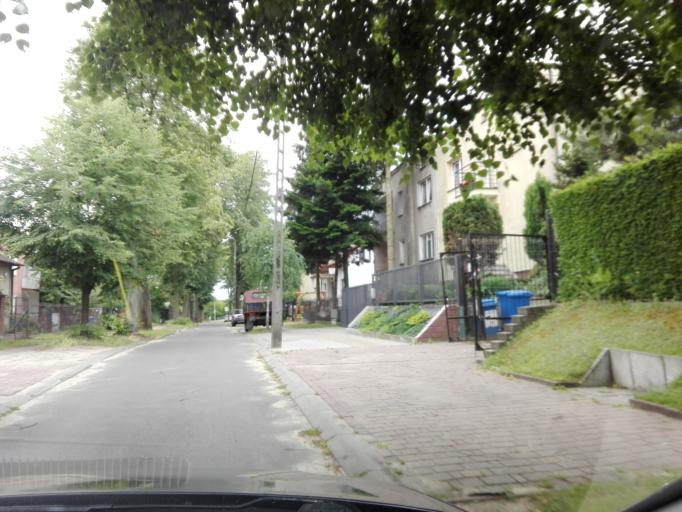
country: PL
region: Lublin Voivodeship
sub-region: Powiat lubelski
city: Lublin
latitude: 51.2200
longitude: 22.5817
